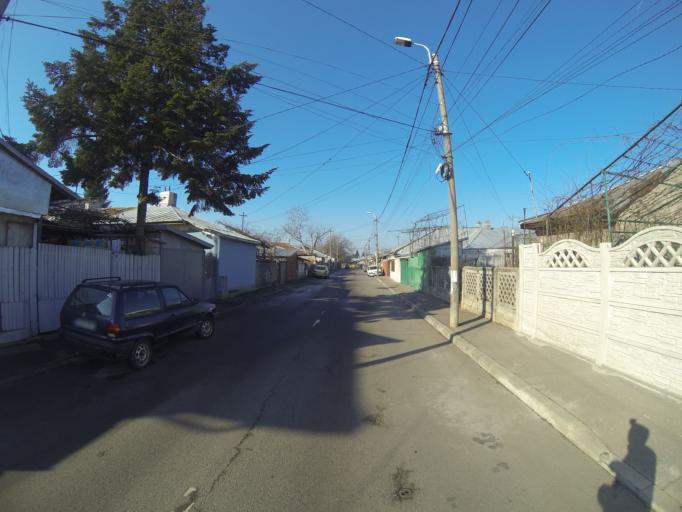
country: RO
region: Bucuresti
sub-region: Municipiul Bucuresti
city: Bucuresti
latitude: 44.3955
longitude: 26.0596
